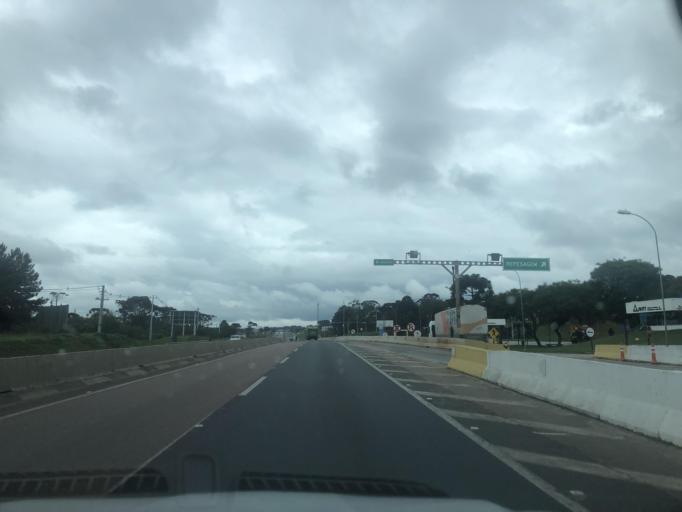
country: BR
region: Parana
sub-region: Araucaria
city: Araucaria
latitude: -25.6736
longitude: -49.3155
